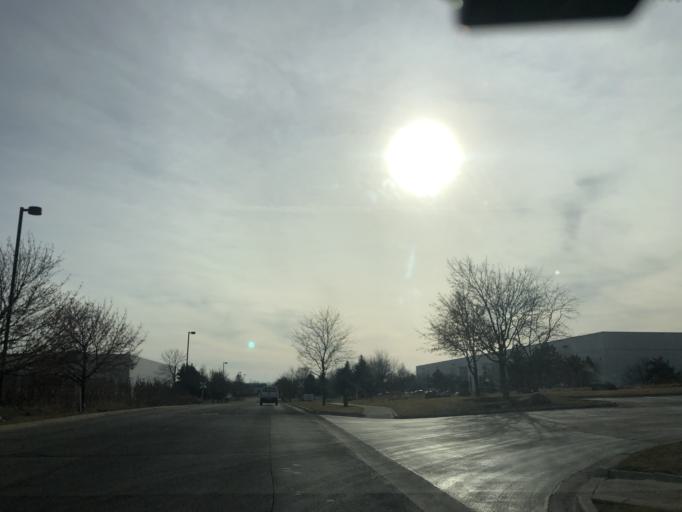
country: US
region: Illinois
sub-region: Cook County
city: Lemont
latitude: 41.7003
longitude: -88.0250
